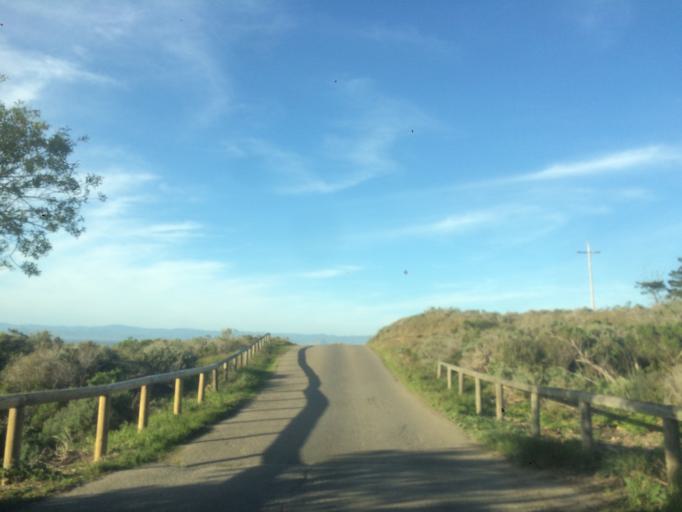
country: US
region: California
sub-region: San Luis Obispo County
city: Los Osos
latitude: 35.2693
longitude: -120.8889
